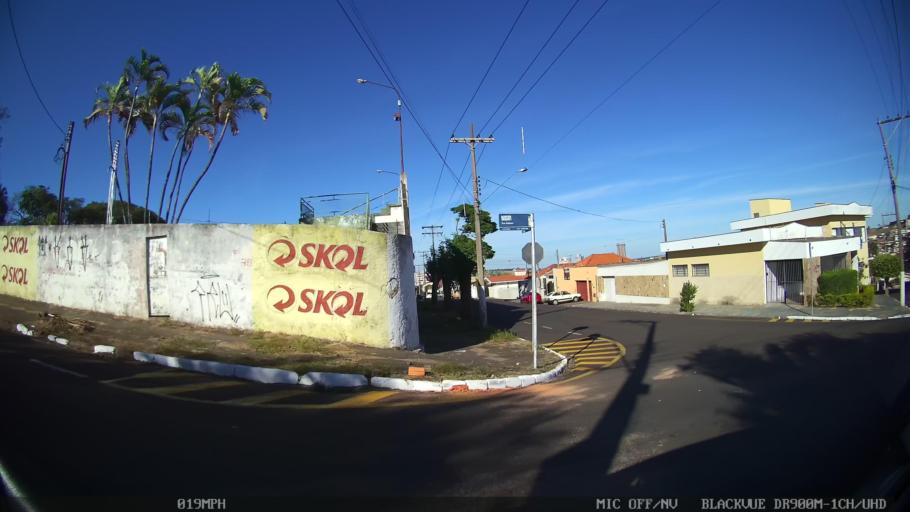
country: BR
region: Sao Paulo
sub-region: Franca
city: Franca
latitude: -20.5416
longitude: -47.4050
